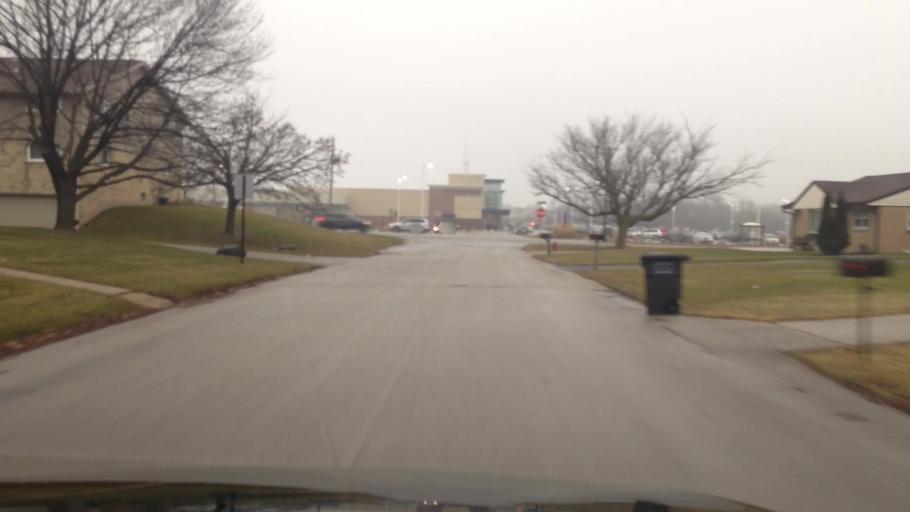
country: US
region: Wisconsin
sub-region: Milwaukee County
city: Greendale
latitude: 42.9608
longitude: -87.9897
